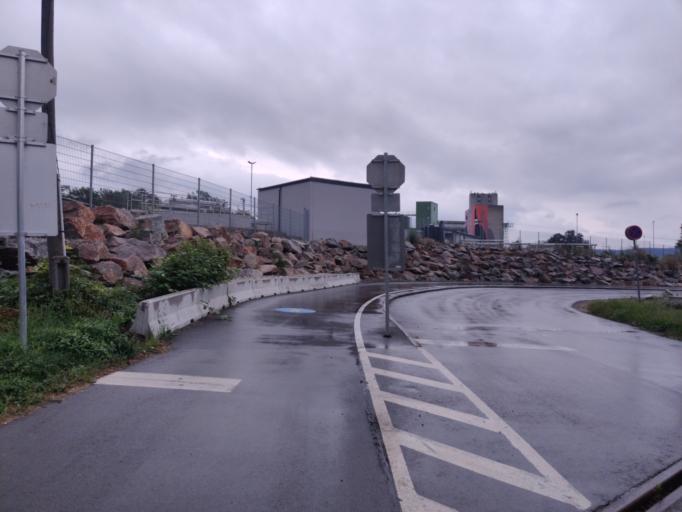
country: AT
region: Lower Austria
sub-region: Politischer Bezirk Korneuburg
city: Korneuburg
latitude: 48.3327
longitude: 16.3315
